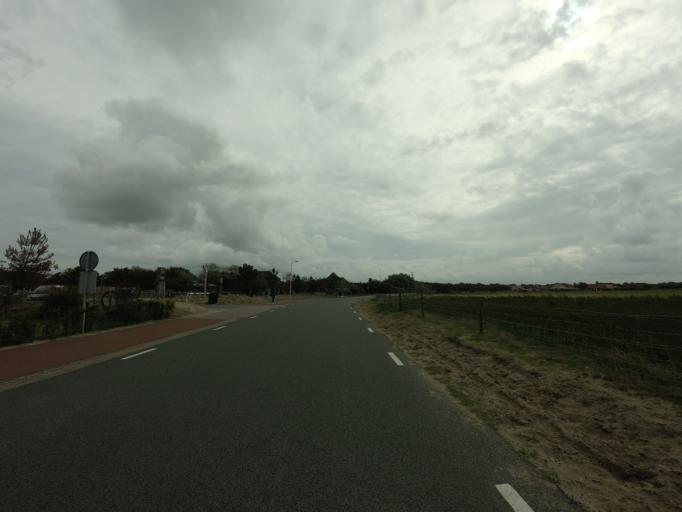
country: NL
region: Friesland
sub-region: Gemeente Ameland
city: Hollum
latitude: 53.4479
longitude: 5.6311
